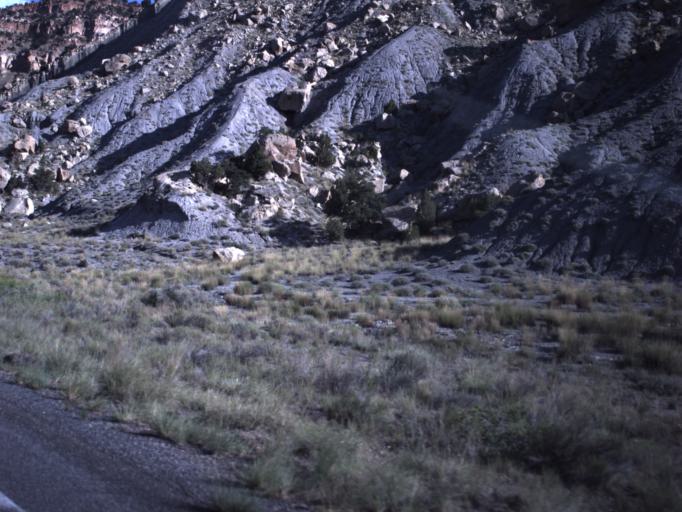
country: US
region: Utah
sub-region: Emery County
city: Huntington
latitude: 39.3888
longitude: -111.0874
